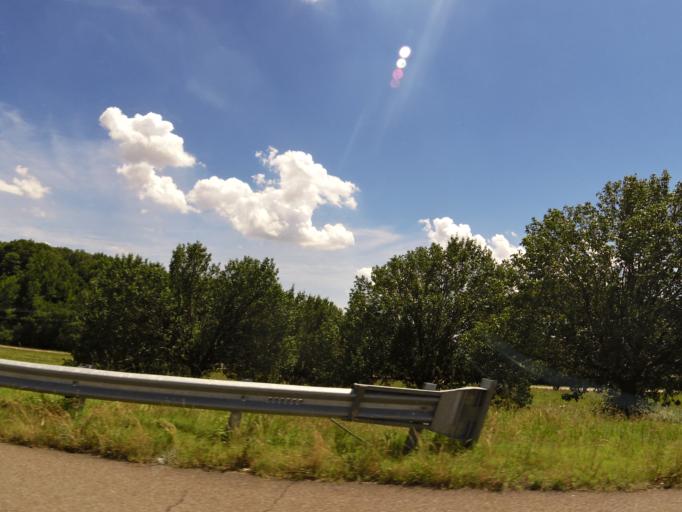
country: US
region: Tennessee
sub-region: Dyer County
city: Dyersburg
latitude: 36.0755
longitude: -89.4980
